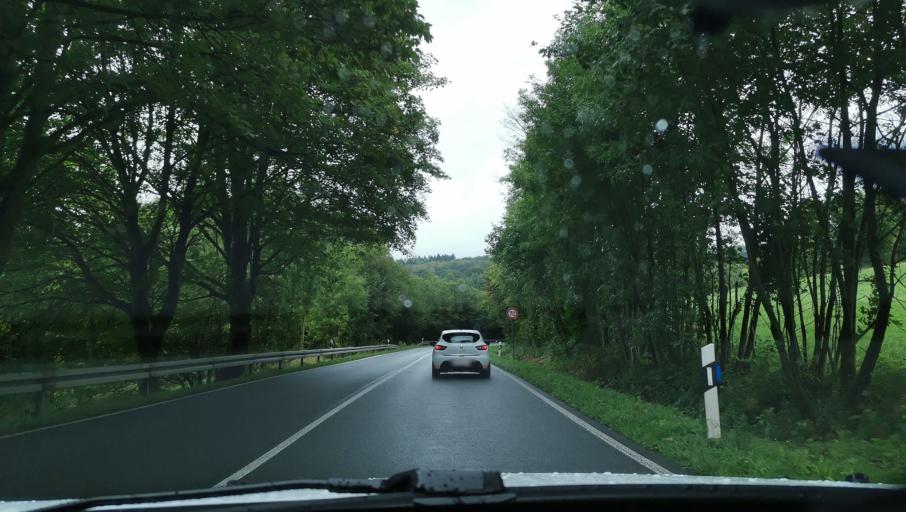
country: DE
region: North Rhine-Westphalia
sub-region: Regierungsbezirk Arnsberg
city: Breckerfeld
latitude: 51.2888
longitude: 7.4568
